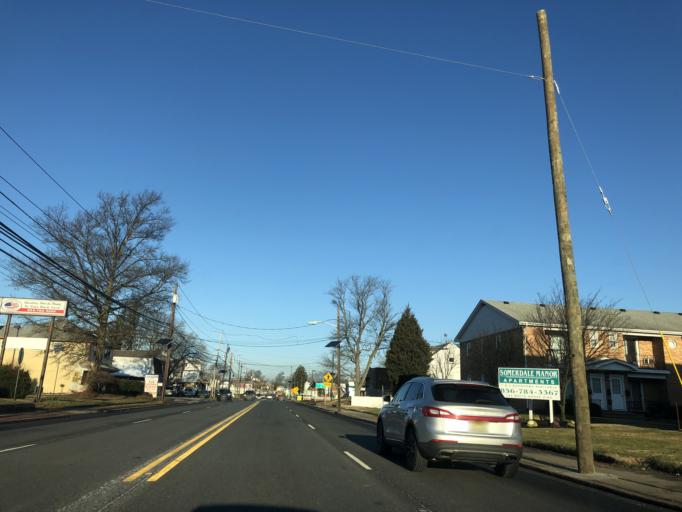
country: US
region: New Jersey
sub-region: Camden County
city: Somerdale
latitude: 39.8419
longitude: -75.0153
